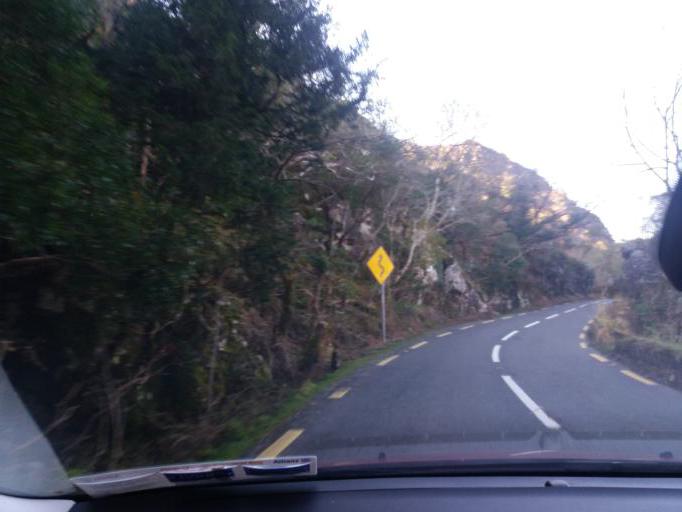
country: IE
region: Munster
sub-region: Ciarrai
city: Cill Airne
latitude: 51.9831
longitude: -9.5700
